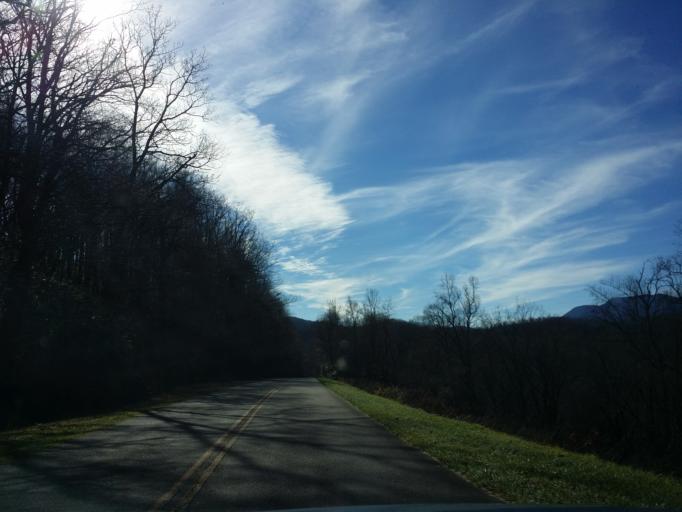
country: US
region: North Carolina
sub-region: McDowell County
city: West Marion
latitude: 35.7609
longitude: -82.1711
